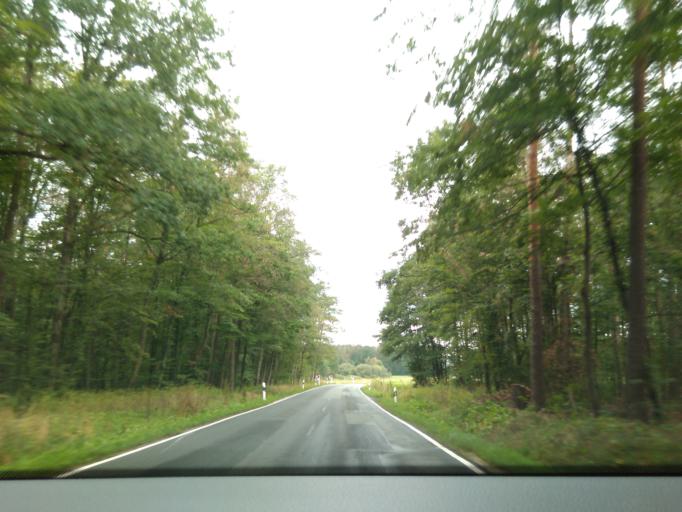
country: DE
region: Bavaria
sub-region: Regierungsbezirk Mittelfranken
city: Hochstadt an der Aisch
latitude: 49.6823
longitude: 10.8063
